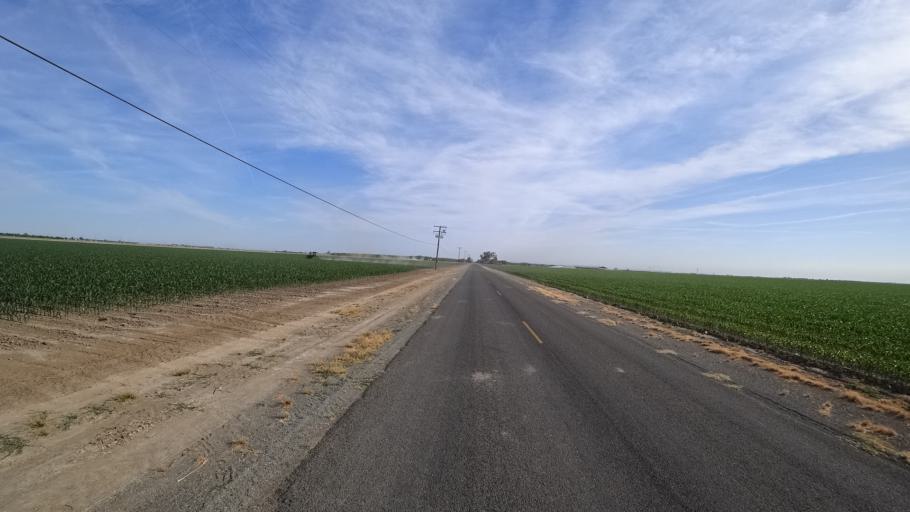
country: US
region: California
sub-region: Kings County
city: Home Garden
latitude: 36.3453
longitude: -119.5472
